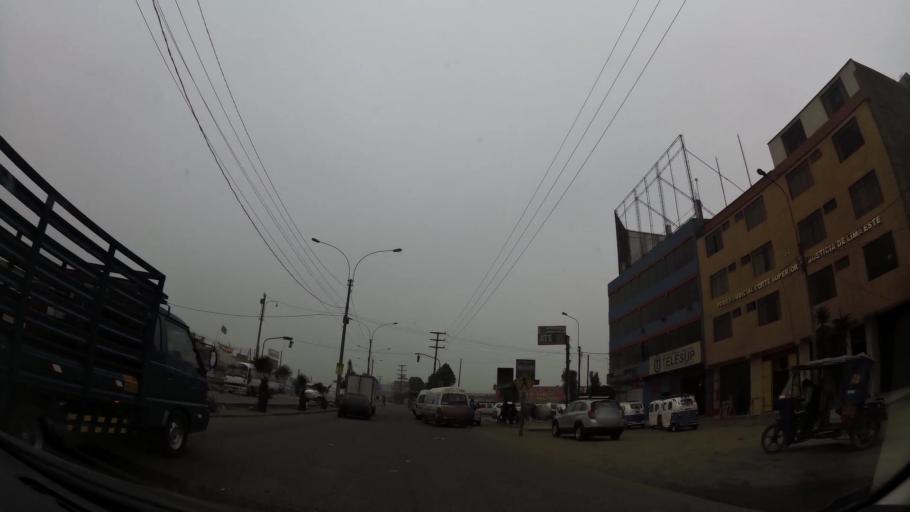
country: PE
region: Lima
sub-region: Lima
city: Santa Maria
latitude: -12.0050
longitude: -76.8449
